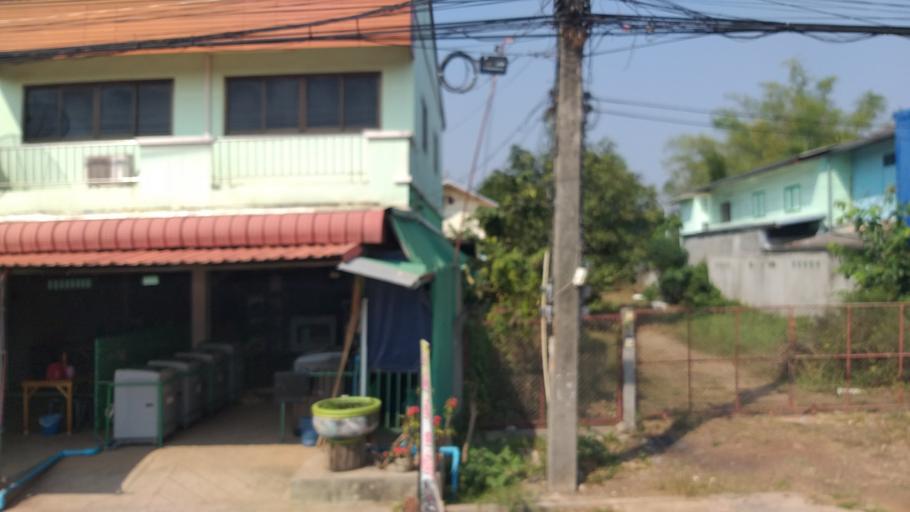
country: TH
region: Changwat Udon Thani
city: Nong Han
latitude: 17.3634
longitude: 103.1128
